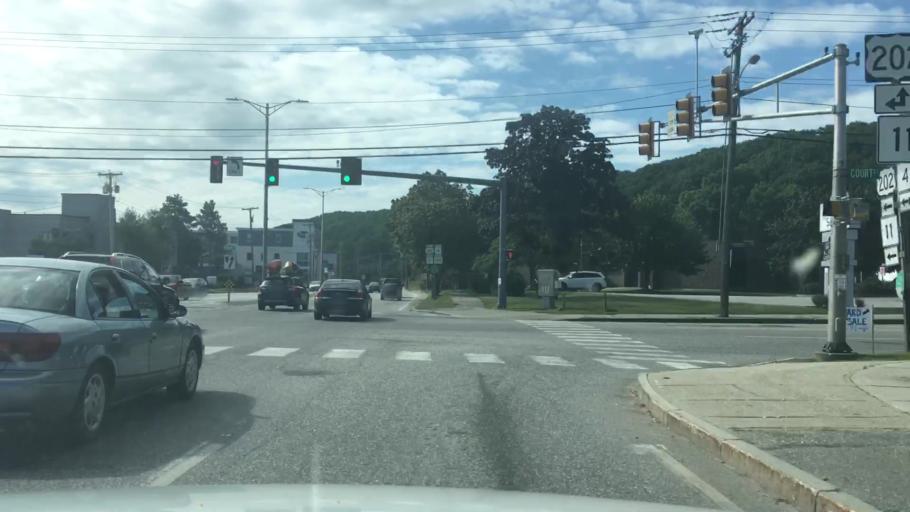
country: US
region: Maine
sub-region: Androscoggin County
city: Auburn
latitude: 44.0982
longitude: -70.2313
